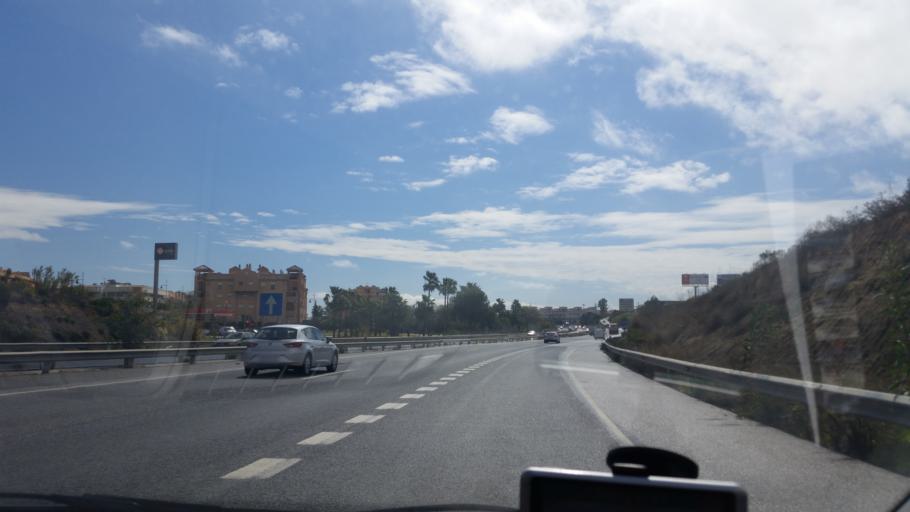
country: ES
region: Andalusia
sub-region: Provincia de Malaga
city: Fuengirola
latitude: 36.5654
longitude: -4.6223
